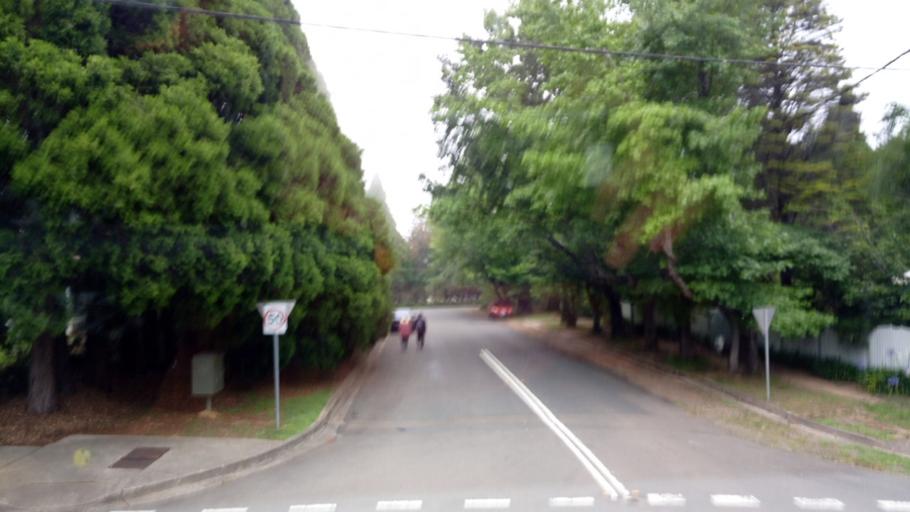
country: AU
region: New South Wales
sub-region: Blue Mountains Municipality
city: Leura
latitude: -33.7209
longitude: 150.3410
